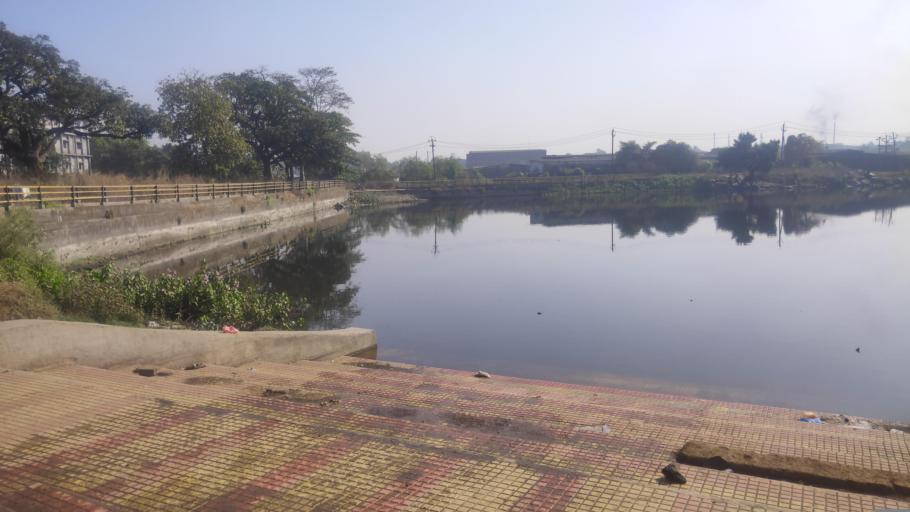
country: IN
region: Maharashtra
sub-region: Thane
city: Bhiwandi
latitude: 19.2942
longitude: 73.0350
